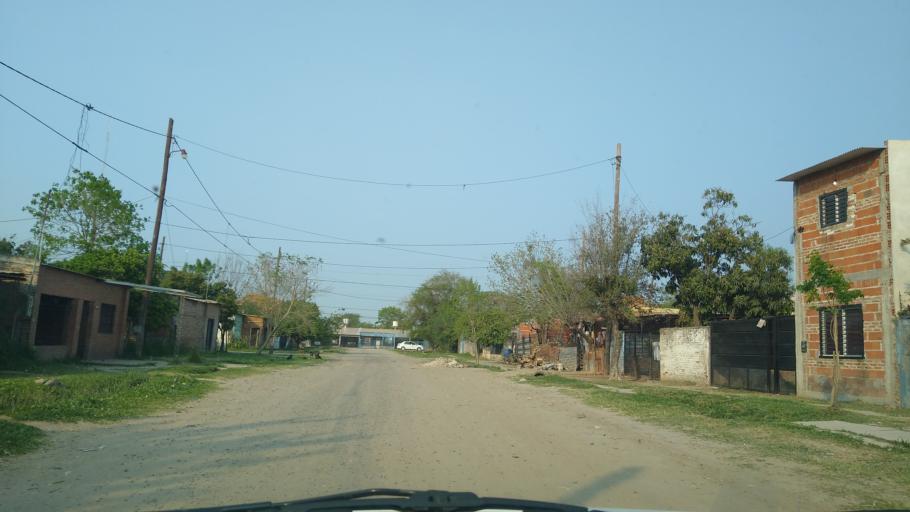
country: AR
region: Chaco
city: Resistencia
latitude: -27.4866
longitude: -58.9736
